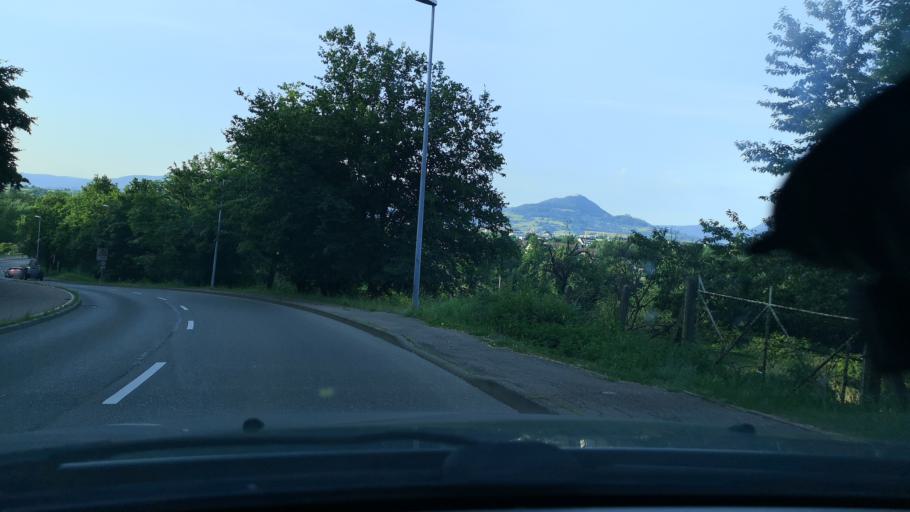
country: DE
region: Baden-Wuerttemberg
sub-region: Regierungsbezirk Stuttgart
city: Kirchheim unter Teck
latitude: 48.6460
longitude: 9.4659
